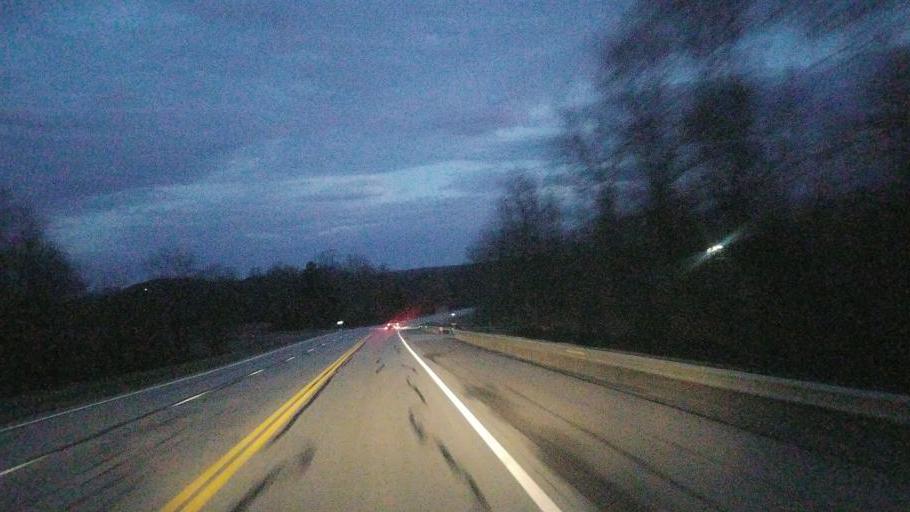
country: US
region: Tennessee
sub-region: Sequatchie County
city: Dunlap
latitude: 35.4895
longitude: -85.4696
